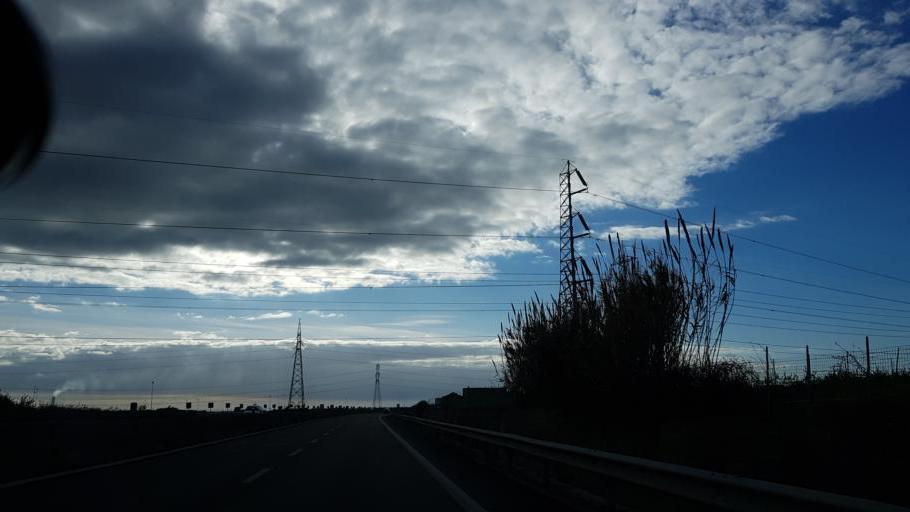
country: IT
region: Apulia
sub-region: Provincia di Brindisi
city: La Rosa
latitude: 40.6087
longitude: 17.9624
